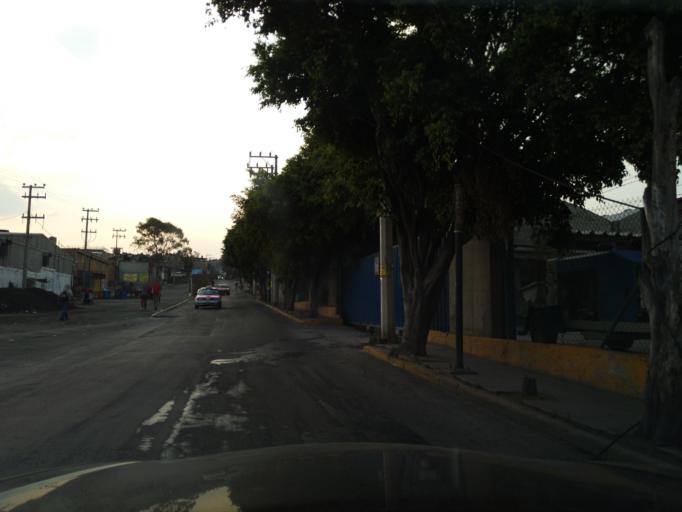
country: MX
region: Mexico City
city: Iztapalapa
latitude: 19.3330
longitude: -99.0818
